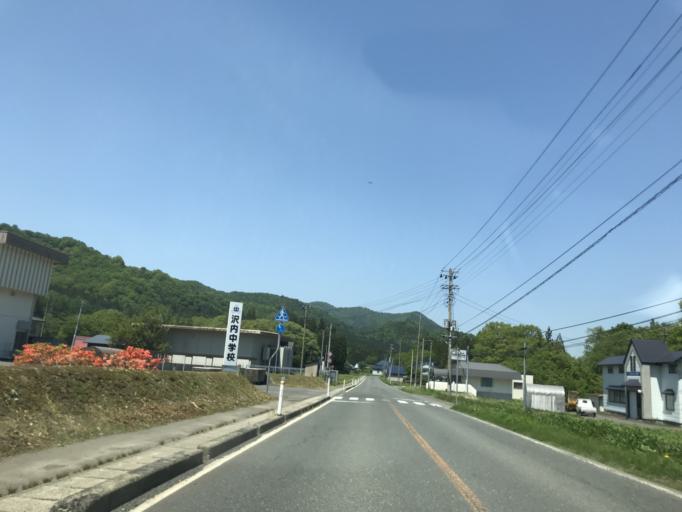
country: JP
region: Akita
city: Yokotemachi
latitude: 39.4370
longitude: 140.7516
